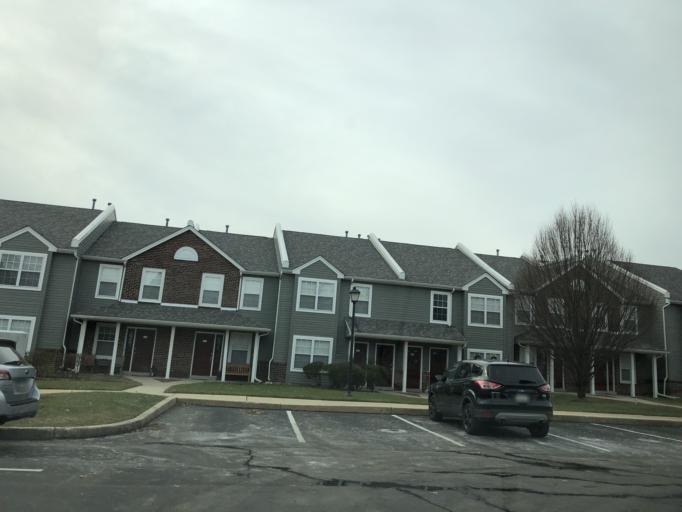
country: US
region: Pennsylvania
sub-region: Chester County
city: Exton
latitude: 40.0293
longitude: -75.6413
